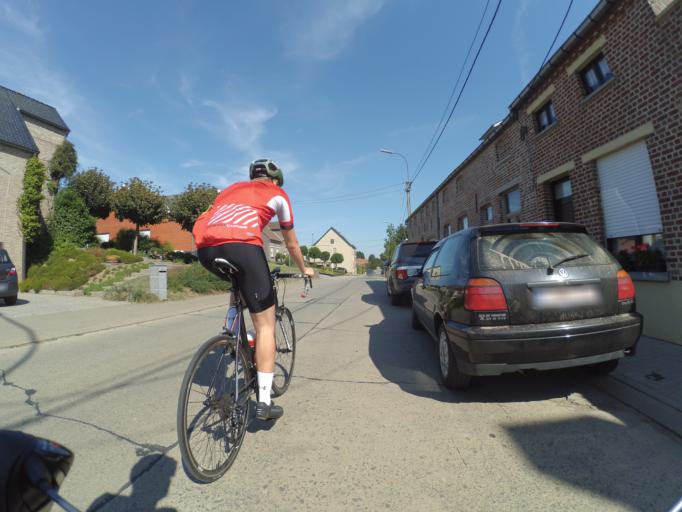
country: BE
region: Flanders
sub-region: Provincie Oost-Vlaanderen
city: Ronse
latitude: 50.7970
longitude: 3.6212
